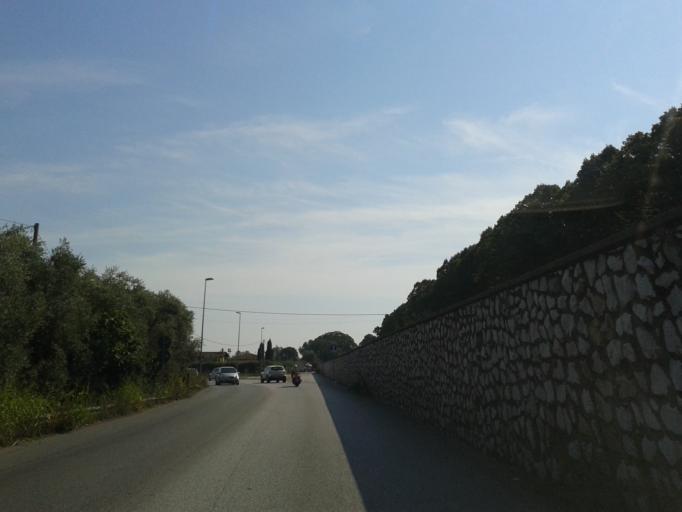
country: IT
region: Tuscany
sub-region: Provincia di Lucca
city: Camaiore
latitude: 43.8978
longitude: 10.2528
